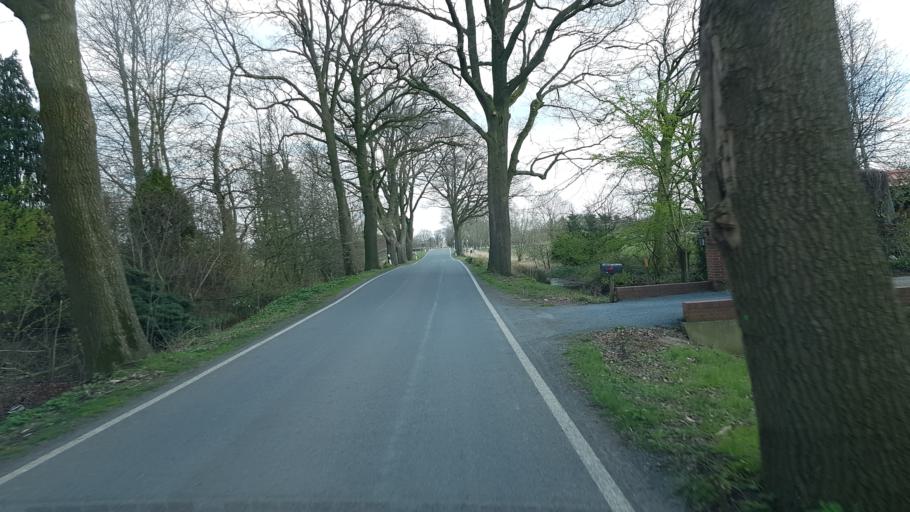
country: DE
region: Lower Saxony
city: Rastede
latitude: 53.3072
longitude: 8.2571
